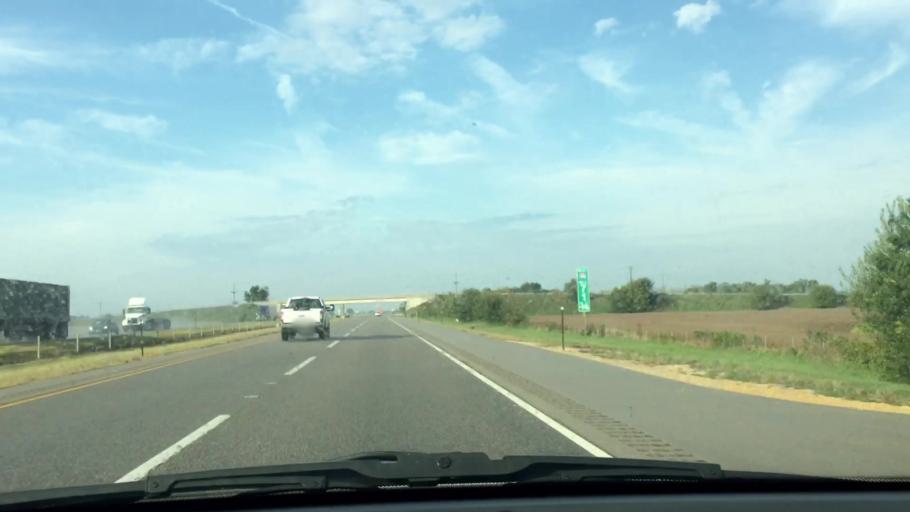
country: US
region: Illinois
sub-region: Ogle County
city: Rochelle
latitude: 41.8771
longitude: -89.1475
